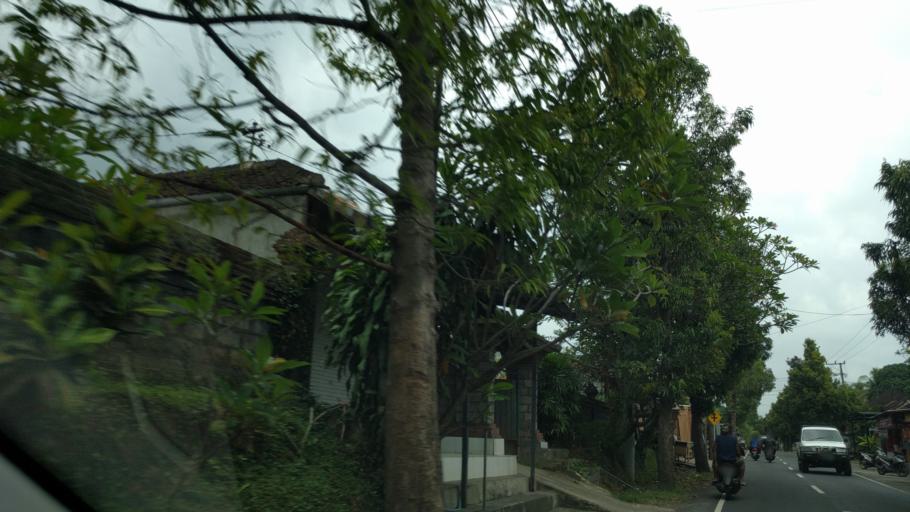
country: ID
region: Bali
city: Banjar Pande
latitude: -8.5119
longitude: 115.2409
